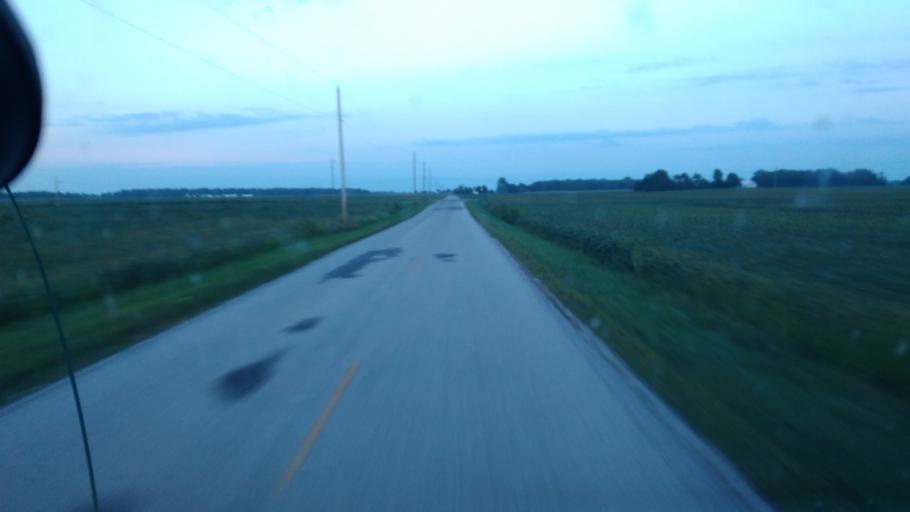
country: US
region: Ohio
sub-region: Hardin County
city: Kenton
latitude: 40.6724
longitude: -83.5167
